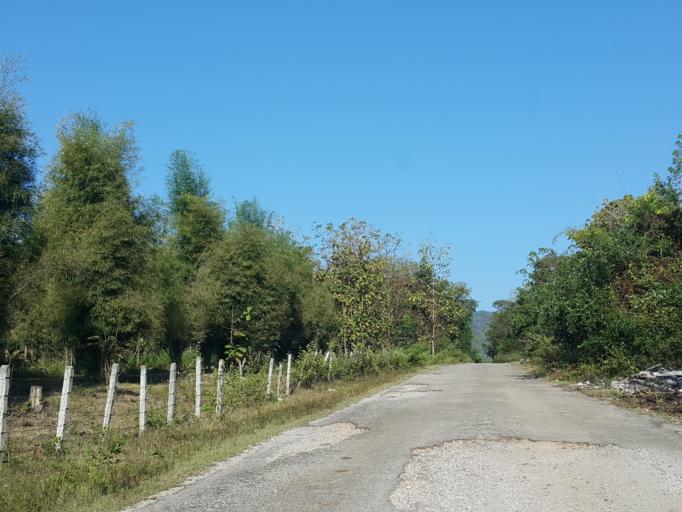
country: TH
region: Lampang
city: Mae Mo
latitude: 18.3014
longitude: 99.6647
